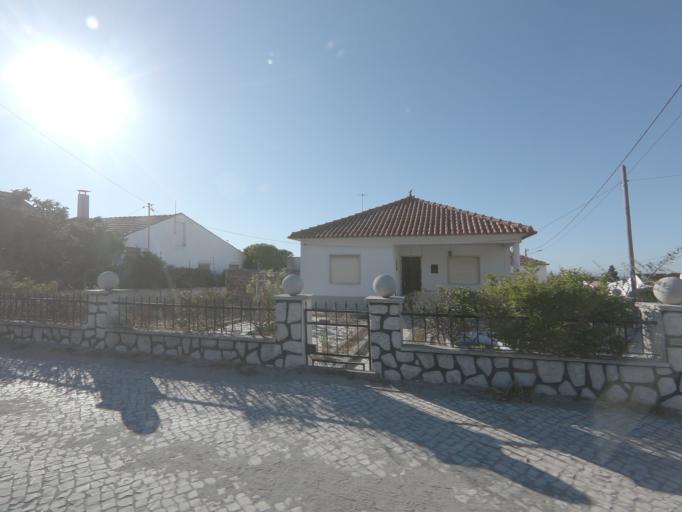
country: PT
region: Setubal
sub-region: Palmela
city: Quinta do Anjo
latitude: 38.5523
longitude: -8.9768
